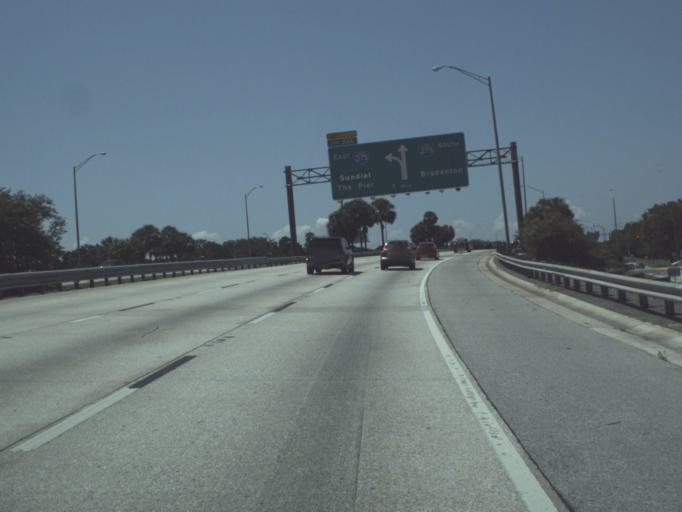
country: US
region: Florida
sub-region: Pinellas County
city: Saint Petersburg
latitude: 27.7938
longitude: -82.6609
